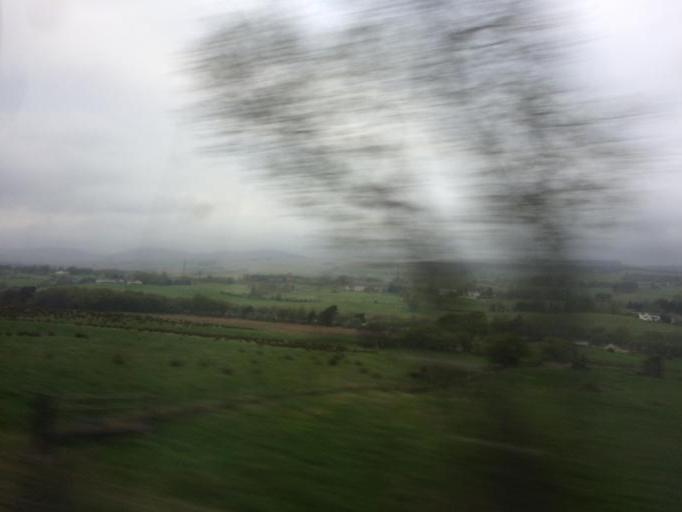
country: GB
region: Scotland
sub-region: North Lanarkshire
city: Cumbernauld
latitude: 55.9803
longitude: -3.9741
